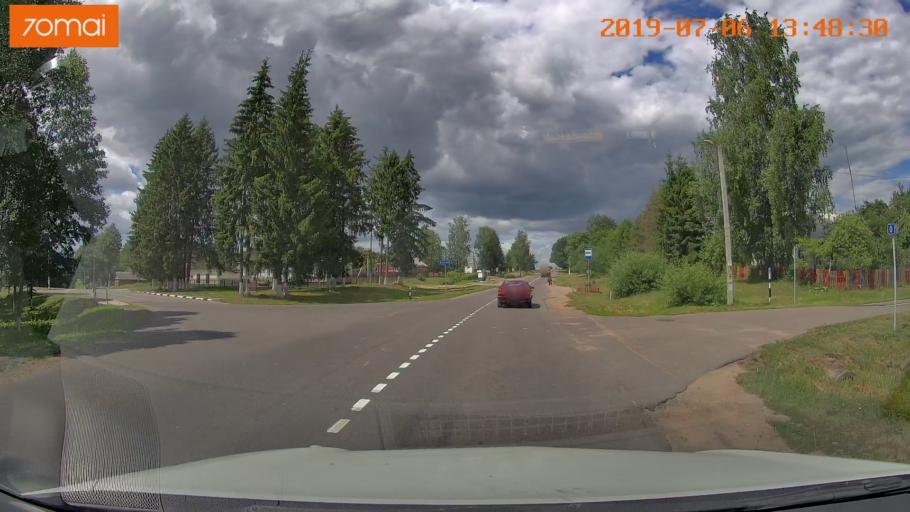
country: BY
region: Minsk
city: Enyerhyetykaw
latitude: 53.6904
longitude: 26.8568
